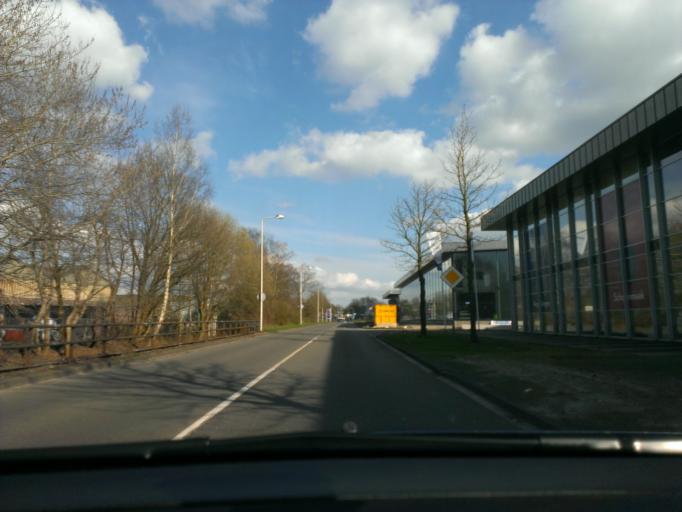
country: NL
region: Overijssel
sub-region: Gemeente Enschede
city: Enschede
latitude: 52.2189
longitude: 6.8656
